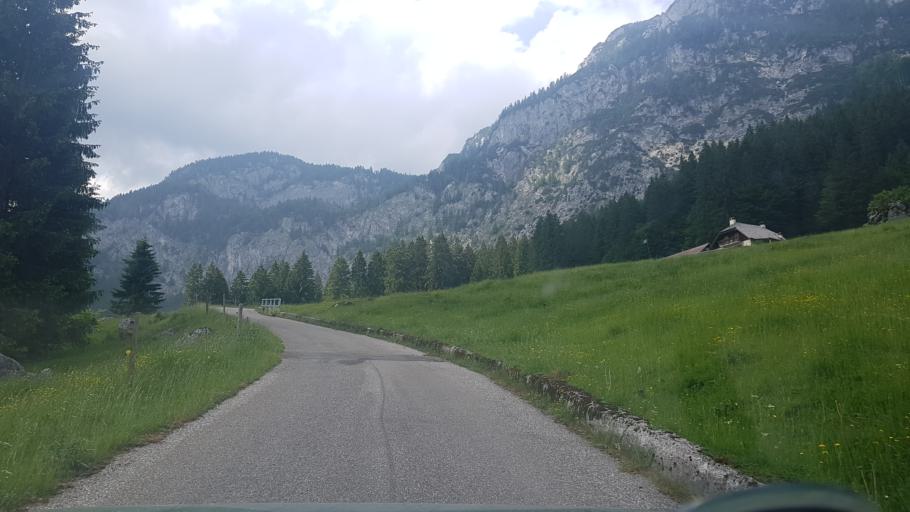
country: IT
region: Friuli Venezia Giulia
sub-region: Provincia di Udine
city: Paularo
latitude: 46.5430
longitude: 13.2045
